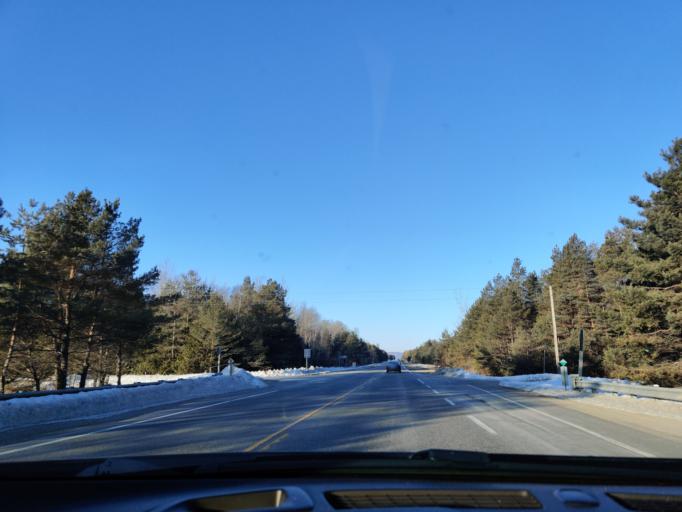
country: CA
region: Ontario
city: Wasaga Beach
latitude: 44.4465
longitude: -79.9530
